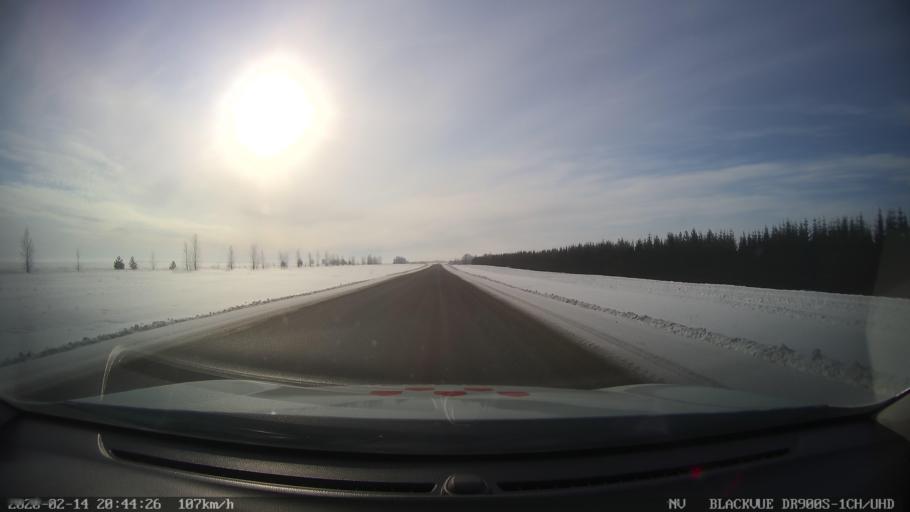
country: RU
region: Tatarstan
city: Kuybyshevskiy Zaton
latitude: 55.2938
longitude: 49.1462
